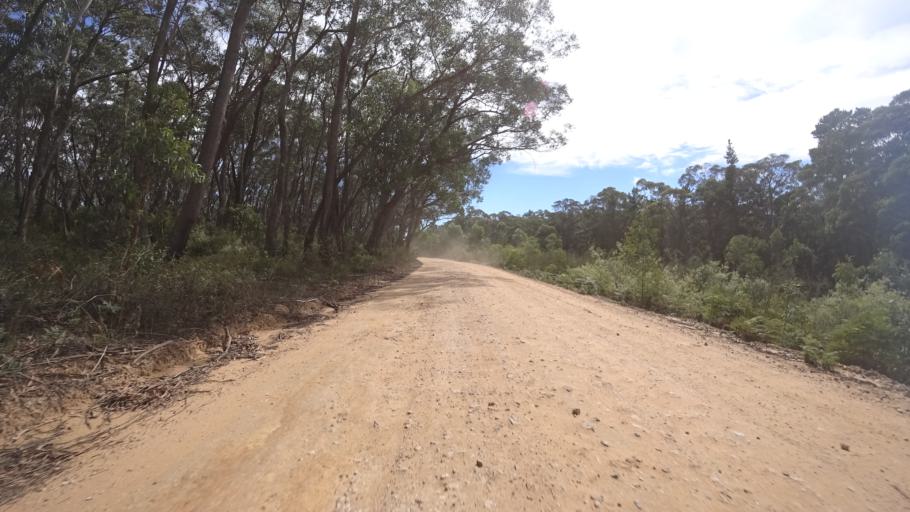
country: AU
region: New South Wales
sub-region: Lithgow
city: Lithgow
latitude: -33.3257
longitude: 150.2482
